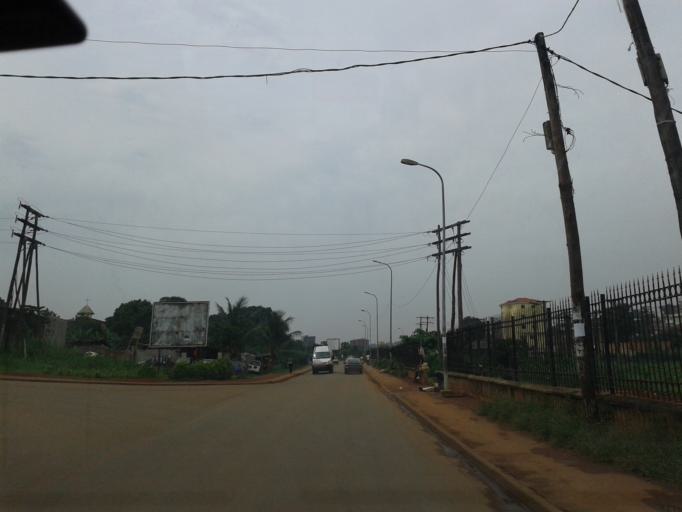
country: CM
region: Centre
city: Yaounde
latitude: 3.8595
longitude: 11.5234
